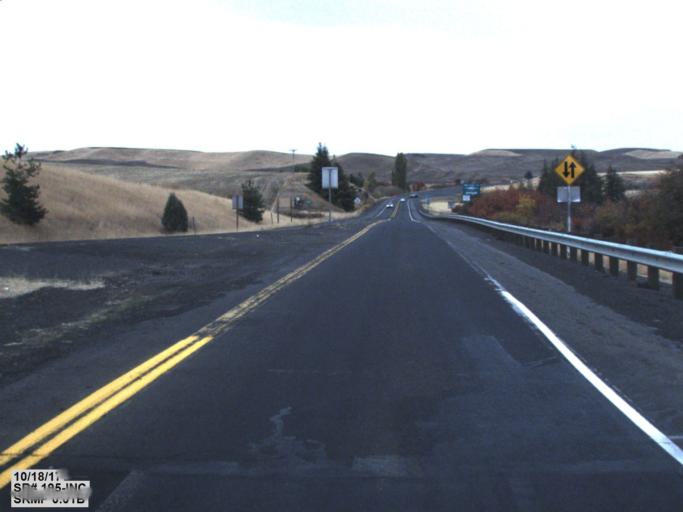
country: US
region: Washington
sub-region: Asotin County
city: Clarkston
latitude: 46.4742
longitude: -117.0399
